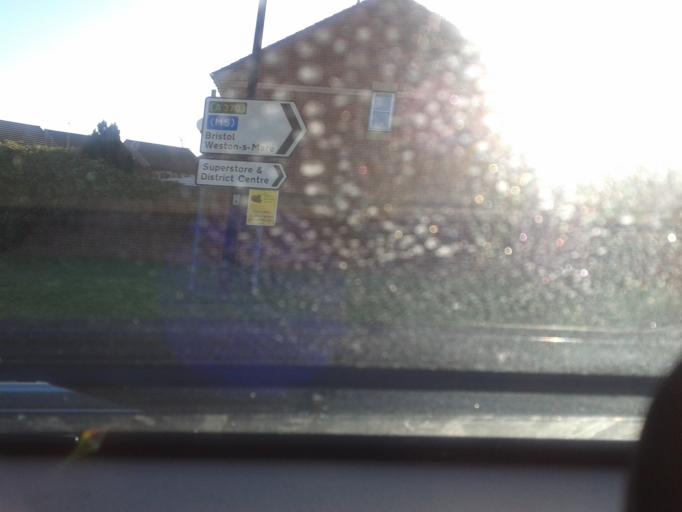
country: GB
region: England
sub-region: North Somerset
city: St. Georges
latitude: 51.3554
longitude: -2.9112
